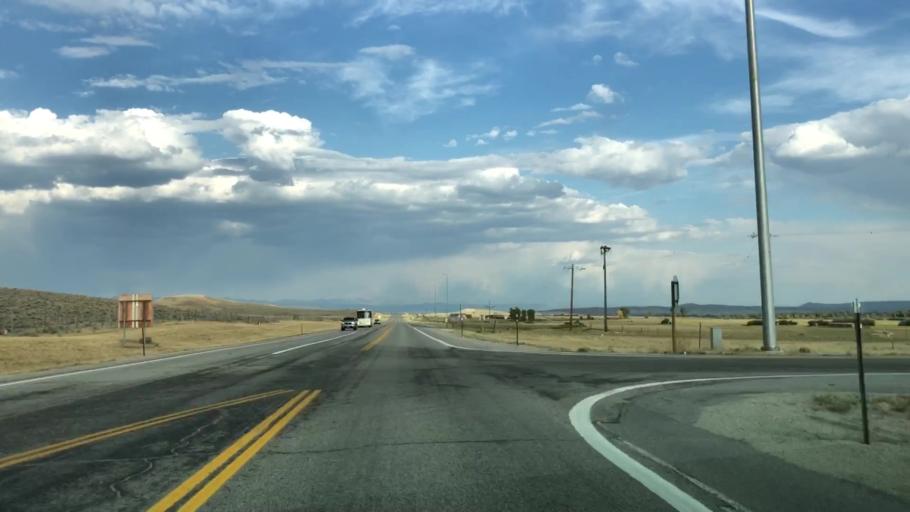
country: US
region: Wyoming
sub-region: Sublette County
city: Pinedale
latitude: 42.8904
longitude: -110.0697
